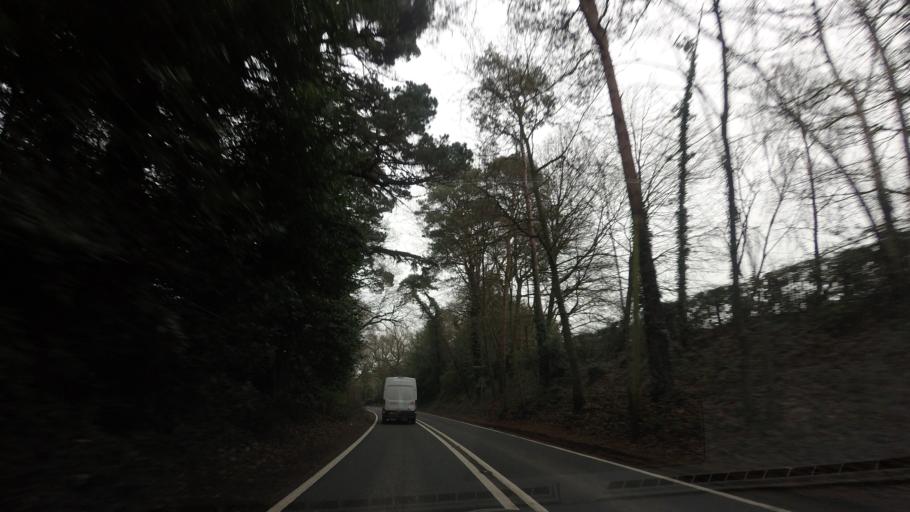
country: GB
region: England
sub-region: Kent
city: Cranbrook
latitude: 51.1210
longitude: 0.5575
